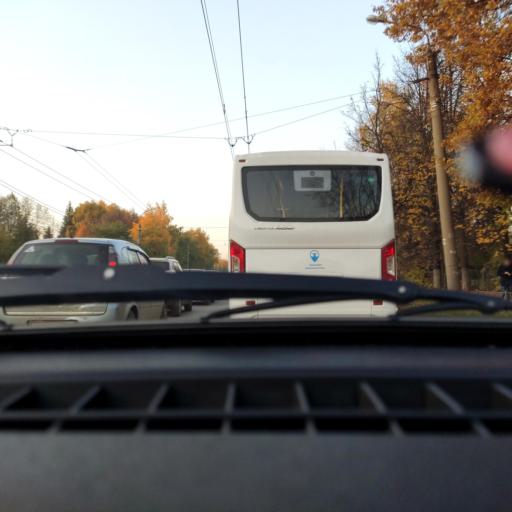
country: RU
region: Bashkortostan
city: Ufa
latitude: 54.7903
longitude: 56.1393
